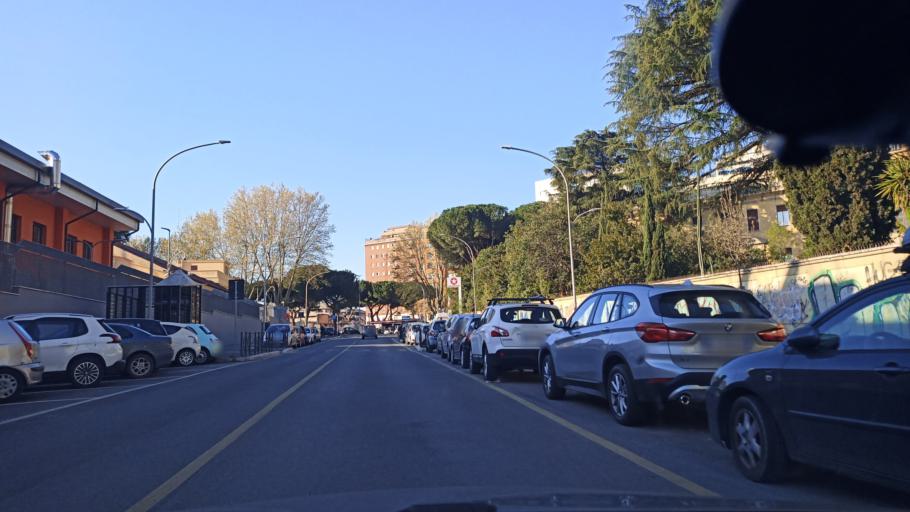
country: IT
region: Latium
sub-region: Citta metropolitana di Roma Capitale
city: Rome
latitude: 41.8778
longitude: 12.5106
